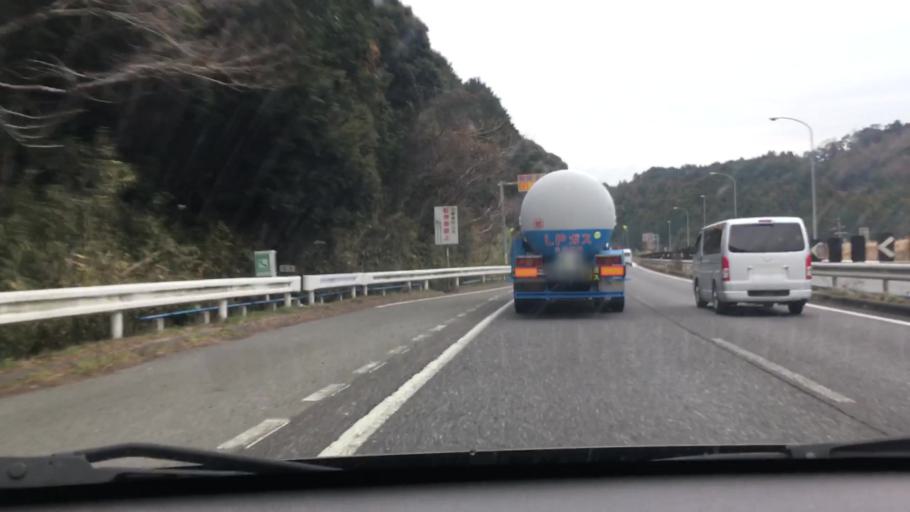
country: JP
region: Mie
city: Kameyama
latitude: 34.8402
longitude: 136.3754
